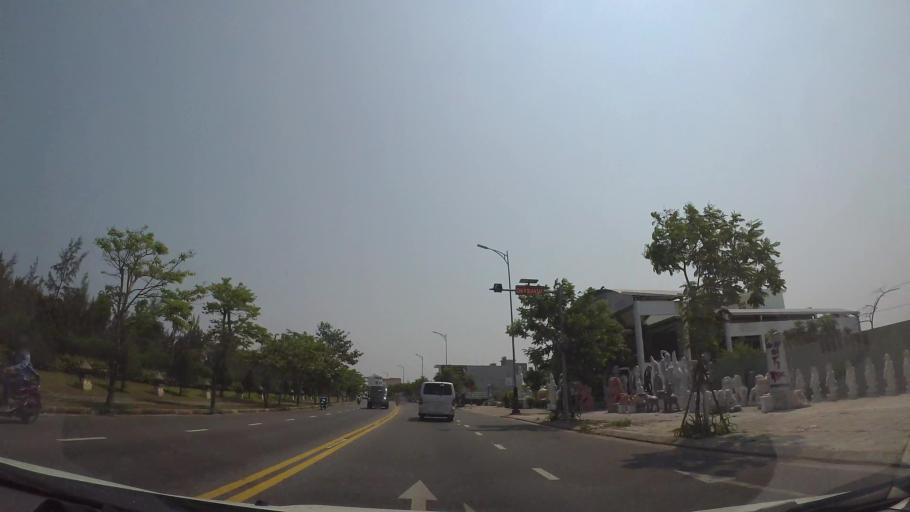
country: VN
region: Da Nang
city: Ngu Hanh Son
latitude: 15.9966
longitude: 108.2676
